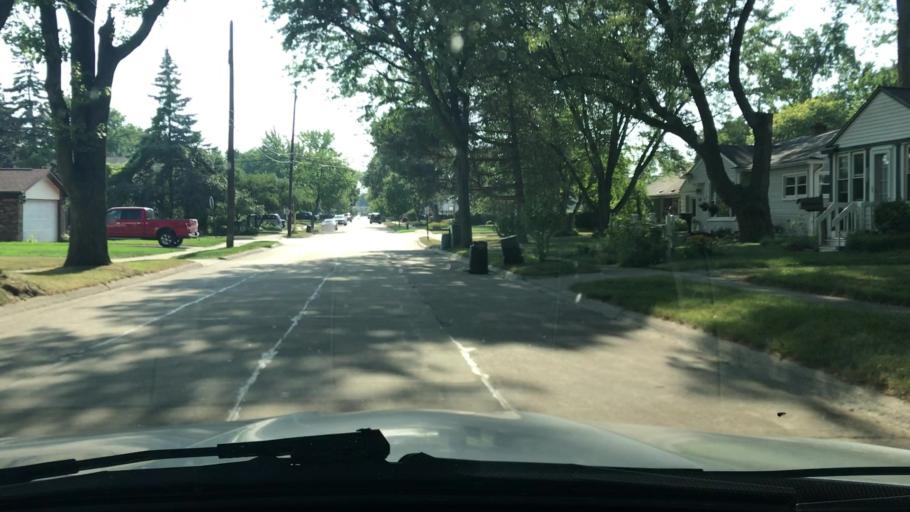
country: US
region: Michigan
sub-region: Oakland County
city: Clawson
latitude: 42.5346
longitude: -83.1519
